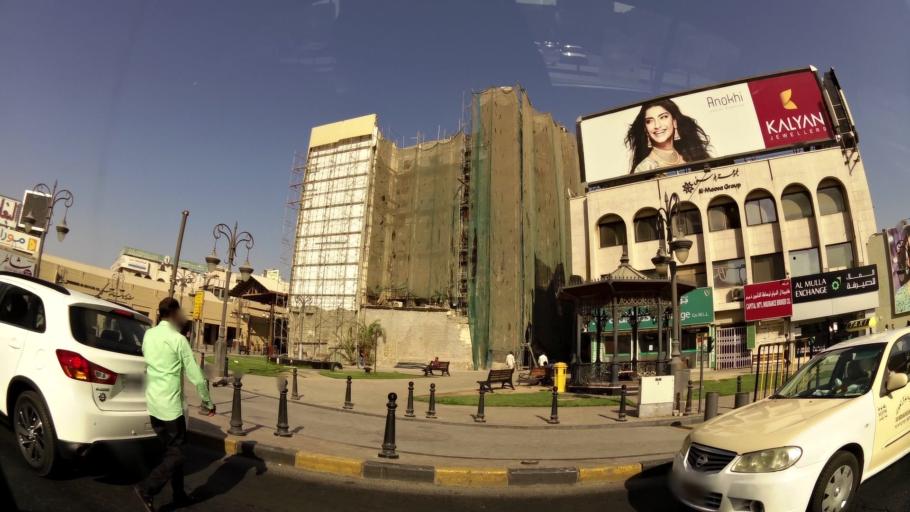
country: KW
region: Al Asimah
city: Kuwait City
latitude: 29.3732
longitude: 47.9756
